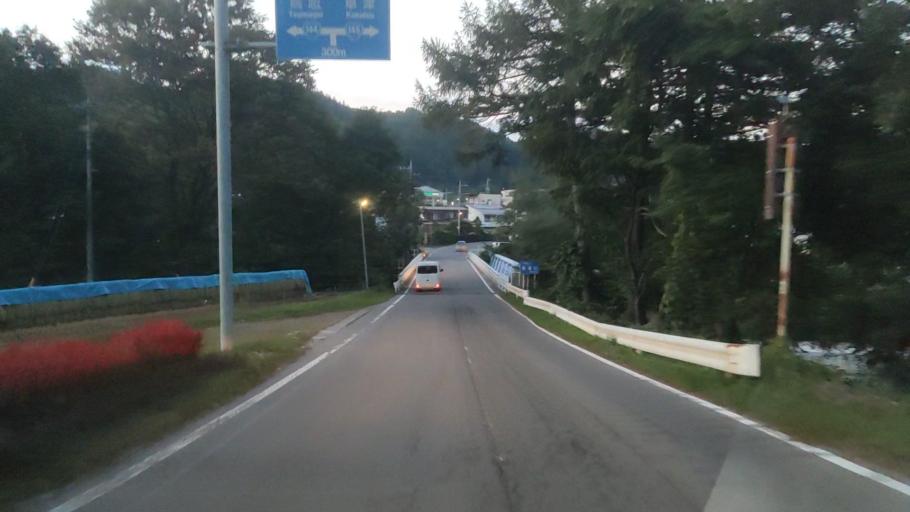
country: JP
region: Gunma
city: Nakanojomachi
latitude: 36.5466
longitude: 138.6048
